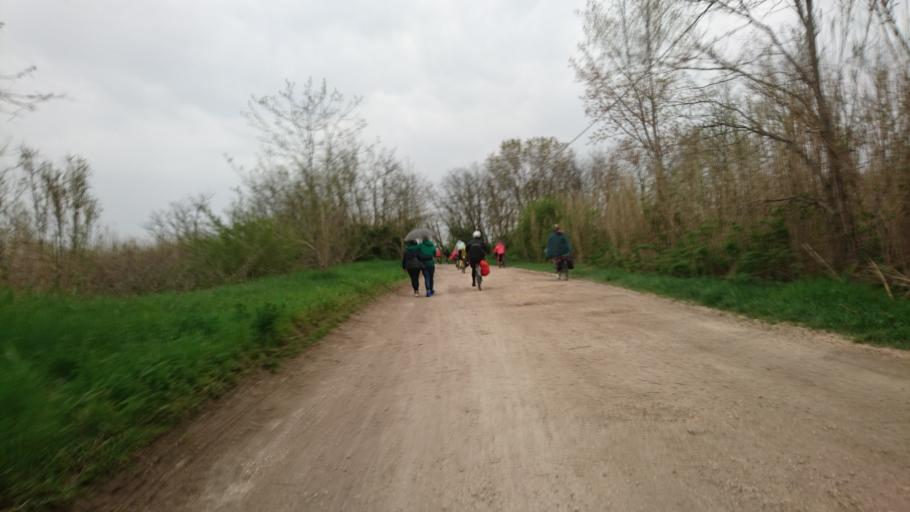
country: IT
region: Veneto
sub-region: Provincia di Venezia
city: Bibione
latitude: 45.6502
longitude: 13.0781
